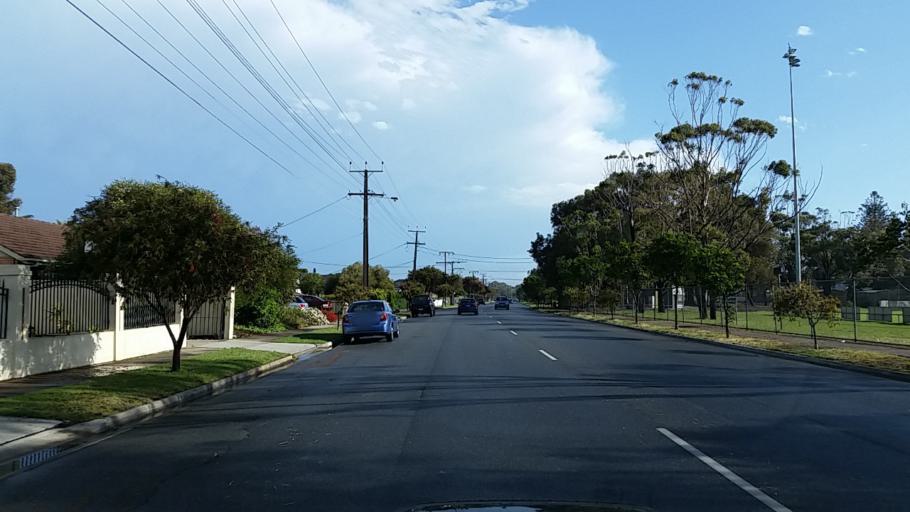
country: AU
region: South Australia
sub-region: Charles Sturt
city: Henley Beach
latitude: -34.9191
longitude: 138.5014
